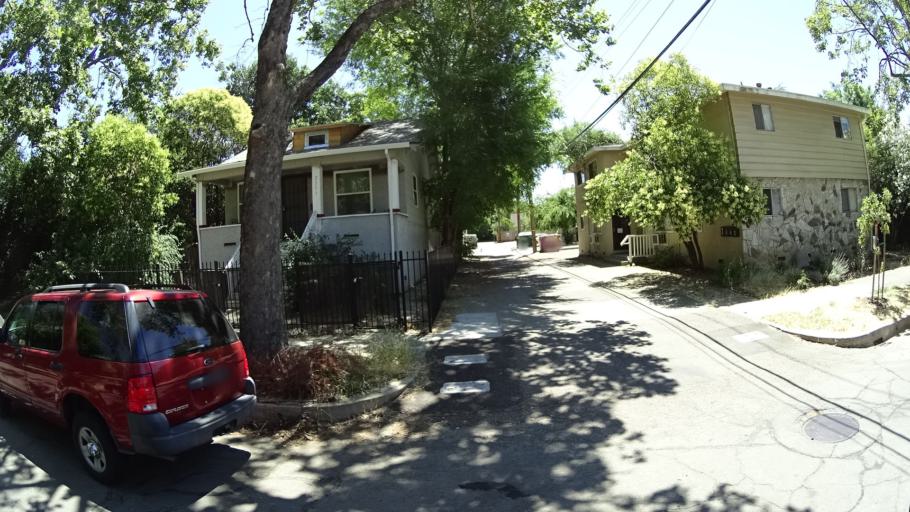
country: US
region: California
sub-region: Sacramento County
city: Sacramento
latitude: 38.5580
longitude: -121.4687
